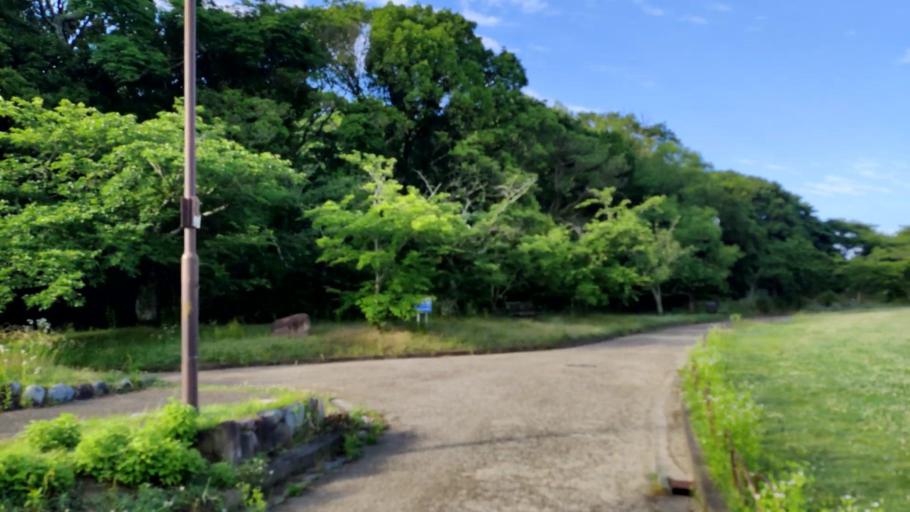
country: JP
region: Hyogo
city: Akashi
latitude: 34.6571
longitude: 134.9939
